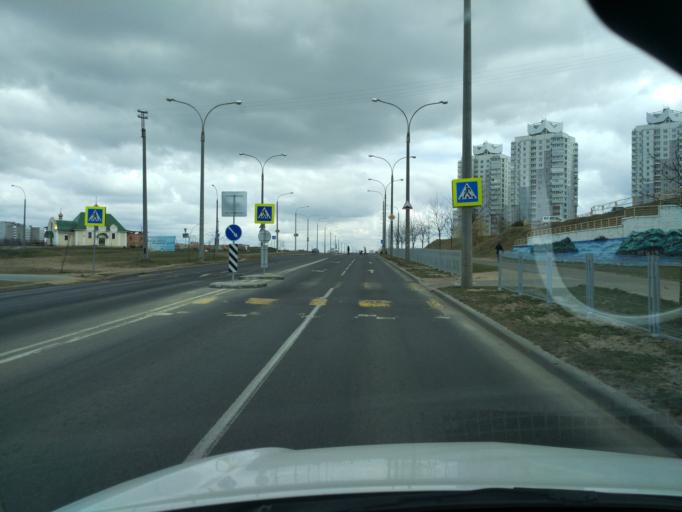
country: BY
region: Minsk
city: Shchomyslitsa
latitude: 53.8503
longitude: 27.4857
